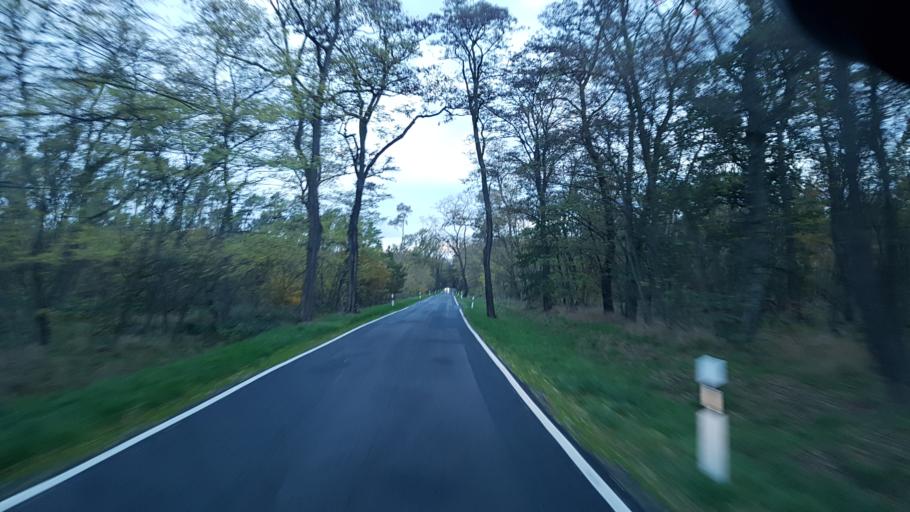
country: DE
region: Brandenburg
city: Muhlberg
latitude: 51.4740
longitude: 13.2387
